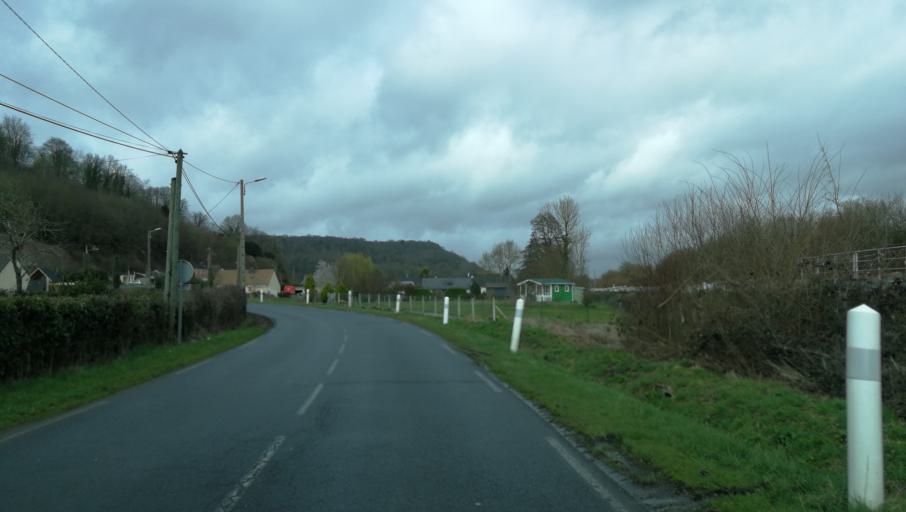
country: FR
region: Haute-Normandie
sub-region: Departement de l'Eure
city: Brionne
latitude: 49.2294
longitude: 0.6943
